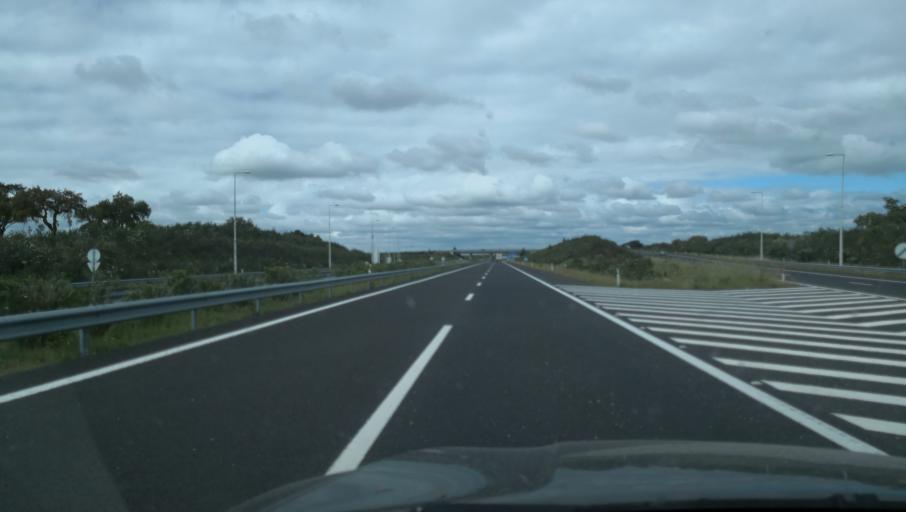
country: PT
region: Santarem
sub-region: Benavente
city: Poceirao
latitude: 38.8980
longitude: -8.7862
